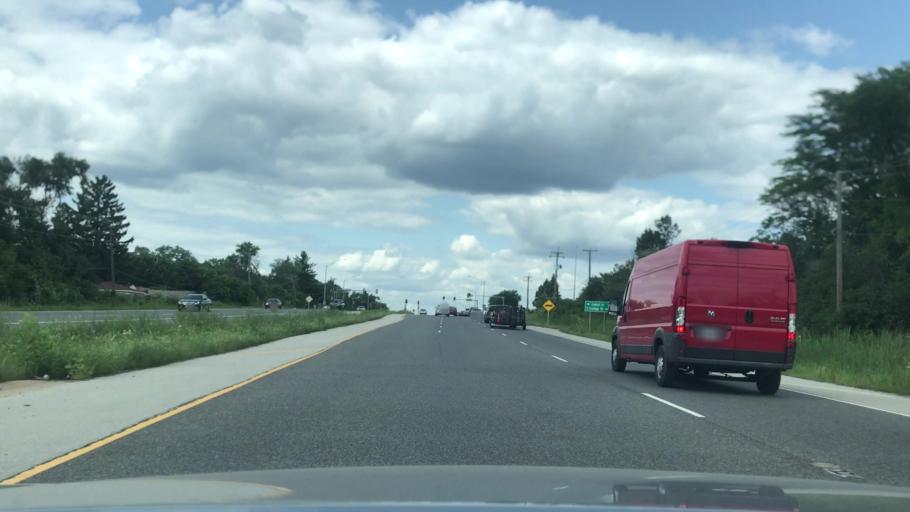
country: US
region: Illinois
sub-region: DuPage County
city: Burr Ridge
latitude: 41.7320
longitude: -87.9439
